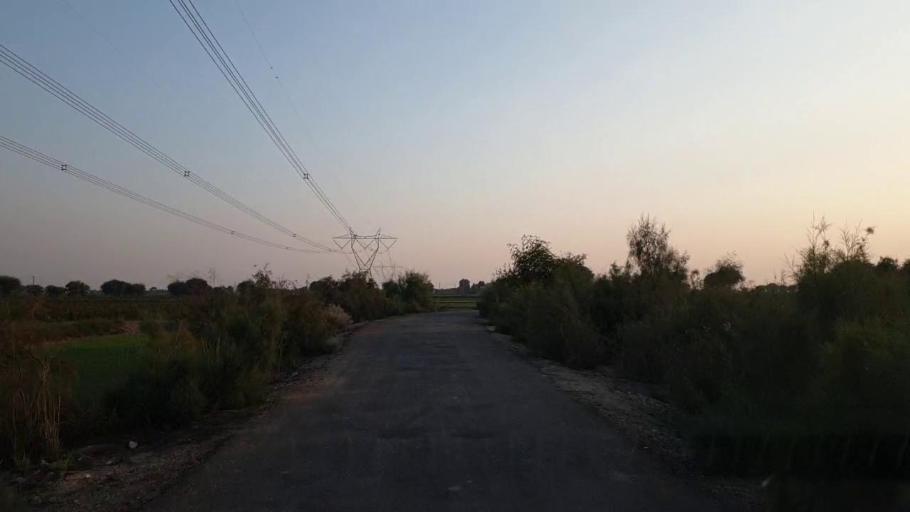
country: PK
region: Sindh
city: Sehwan
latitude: 26.4479
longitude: 67.7626
